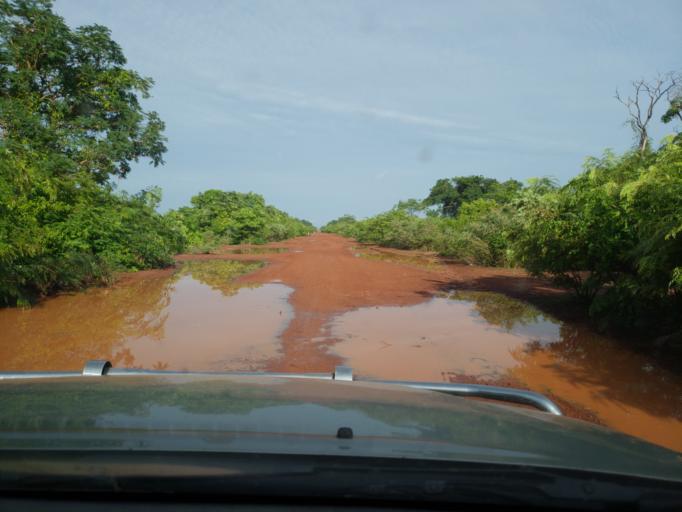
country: ML
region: Sikasso
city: Koutiala
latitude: 12.4175
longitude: -5.7113
